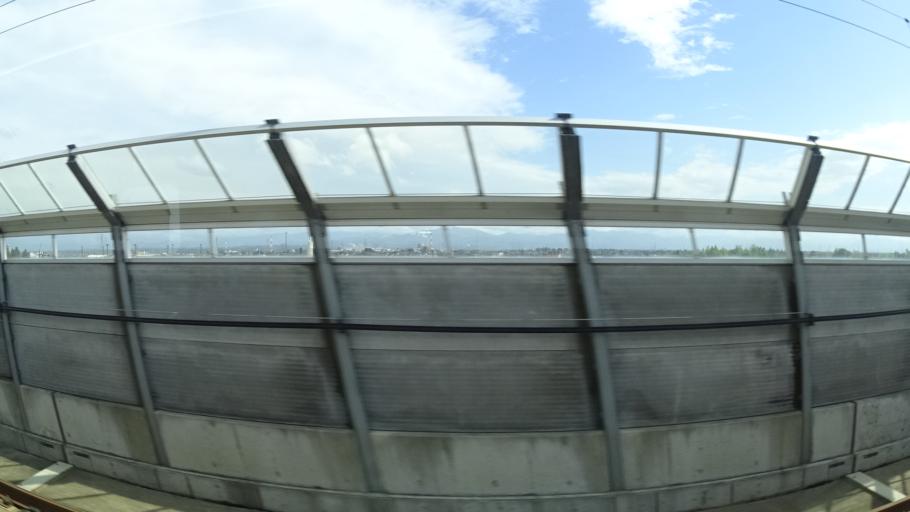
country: JP
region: Toyama
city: Takaoka
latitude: 36.7269
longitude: 137.0032
